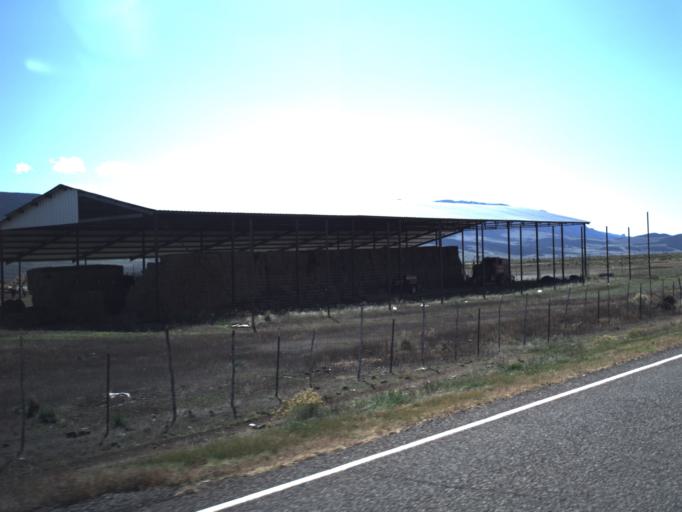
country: US
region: Utah
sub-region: Sevier County
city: Monroe
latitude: 38.4473
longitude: -111.9156
